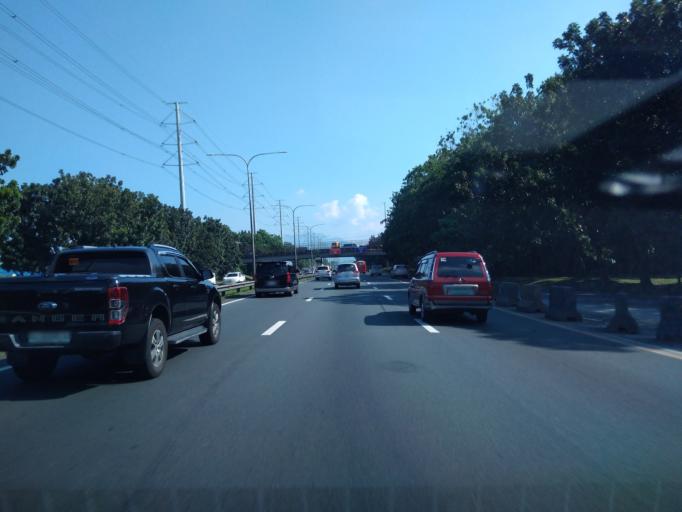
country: PH
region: Calabarzon
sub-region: Province of Laguna
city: Cabuyao
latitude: 14.2423
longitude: 121.1109
